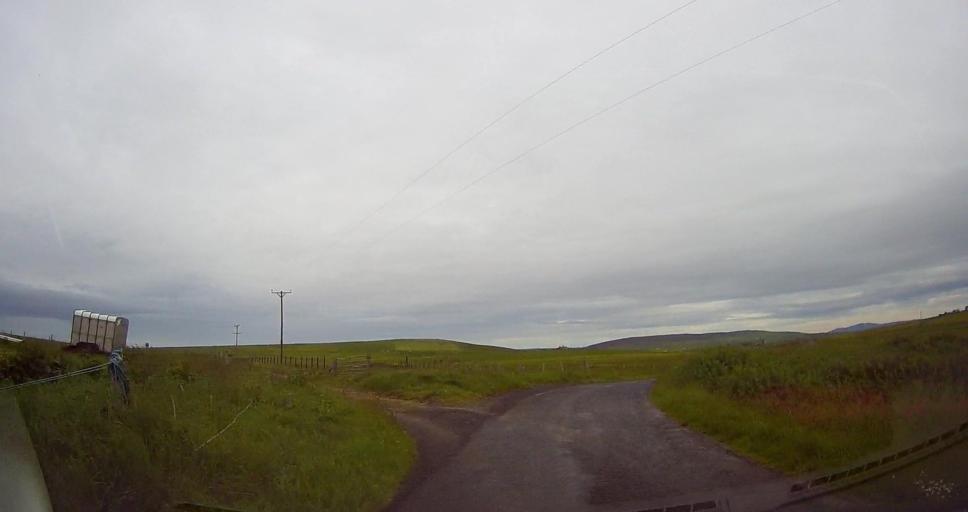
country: GB
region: Scotland
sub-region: Orkney Islands
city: Stromness
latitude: 59.1251
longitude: -3.2802
